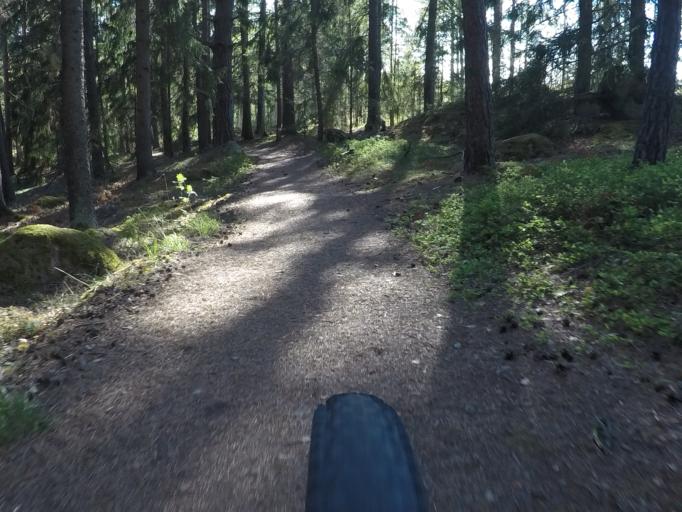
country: SE
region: Soedermanland
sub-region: Eskilstuna Kommun
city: Eskilstuna
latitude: 59.4061
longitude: 16.5255
